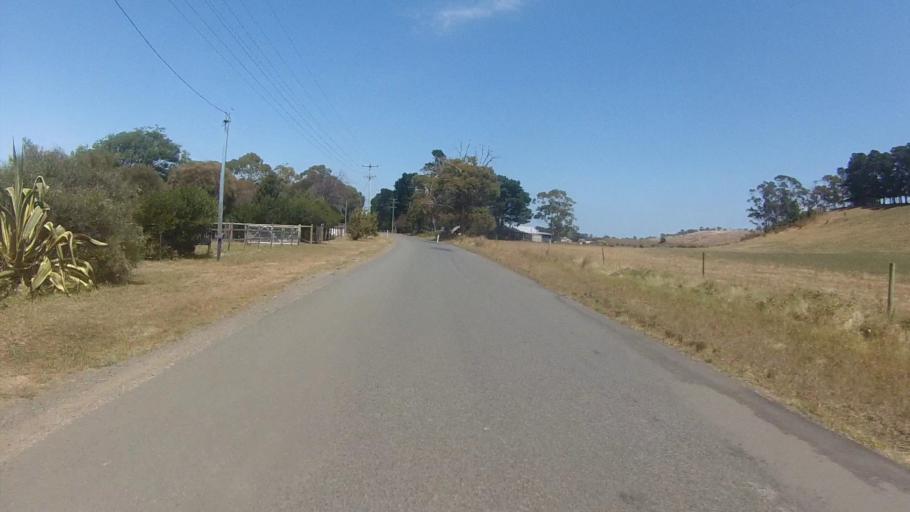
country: AU
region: Tasmania
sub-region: Sorell
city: Sorell
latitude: -42.8231
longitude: 147.8593
